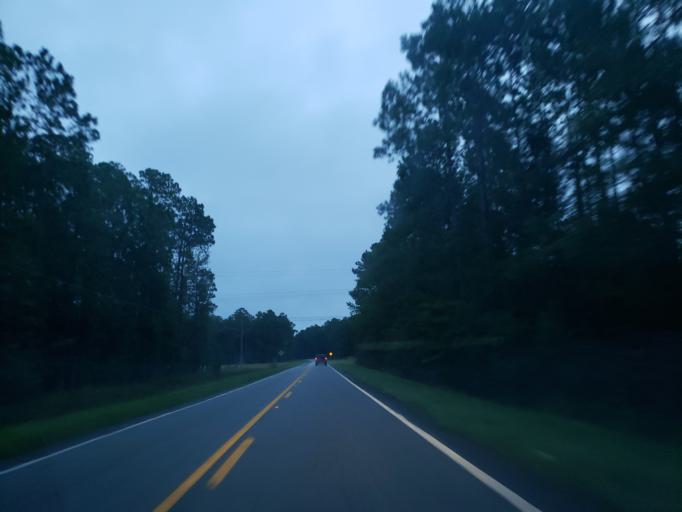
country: US
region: Georgia
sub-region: Chatham County
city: Bloomingdale
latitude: 32.0876
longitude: -81.3576
